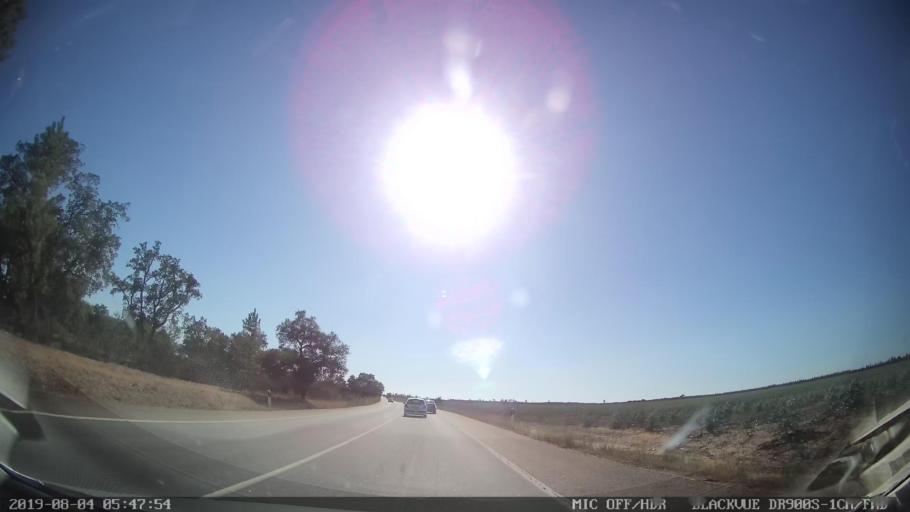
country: PT
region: Portalegre
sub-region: Gaviao
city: Gaviao
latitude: 39.4473
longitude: -7.8169
